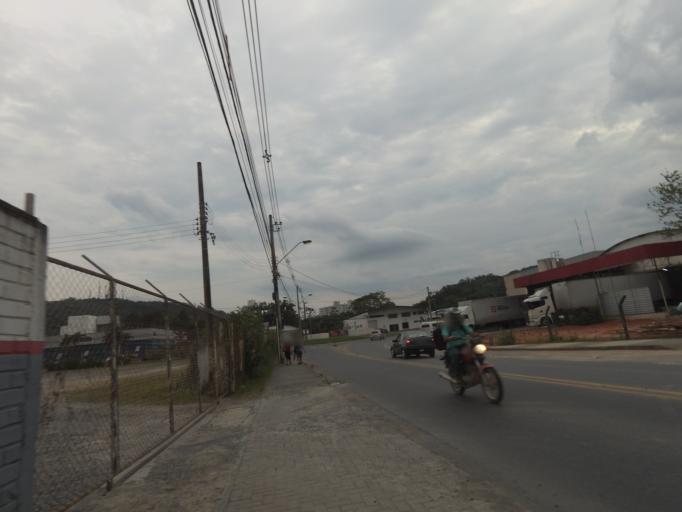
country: BR
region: Santa Catarina
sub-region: Blumenau
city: Blumenau
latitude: -26.8924
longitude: -49.0632
